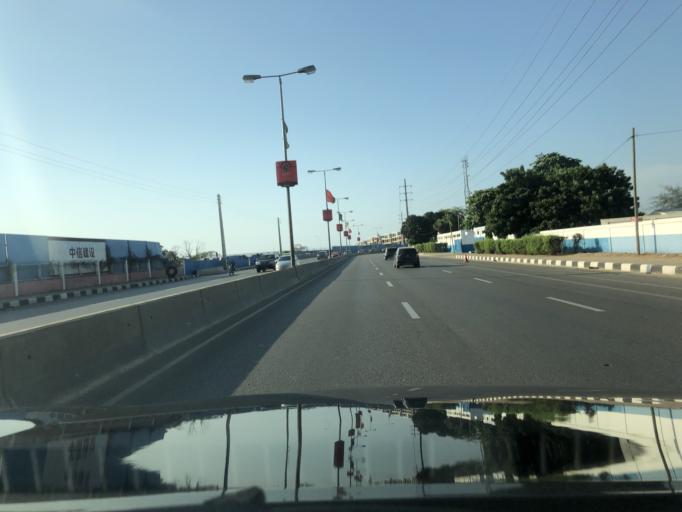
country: AO
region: Luanda
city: Luanda
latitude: -8.9010
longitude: 13.1768
